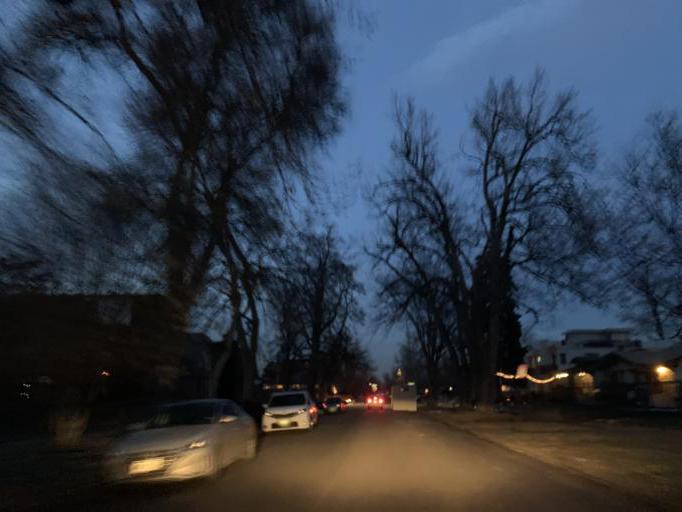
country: US
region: Colorado
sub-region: Jefferson County
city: Edgewater
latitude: 39.7759
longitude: -105.0416
